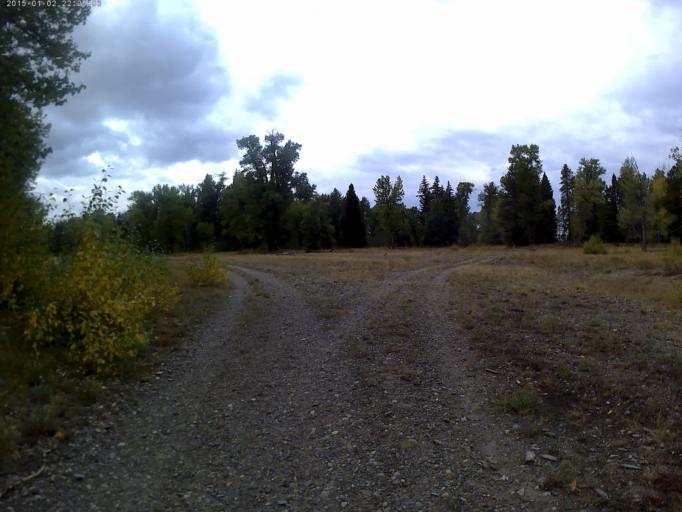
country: US
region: Wyoming
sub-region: Teton County
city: Moose Wilson Road
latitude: 43.8951
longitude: -110.6004
